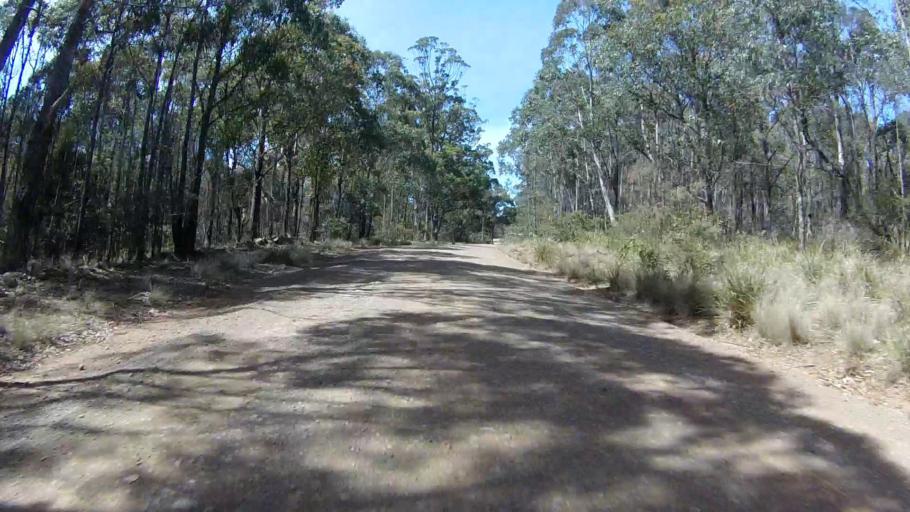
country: AU
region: Tasmania
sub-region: Sorell
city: Sorell
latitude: -42.6657
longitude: 147.7299
